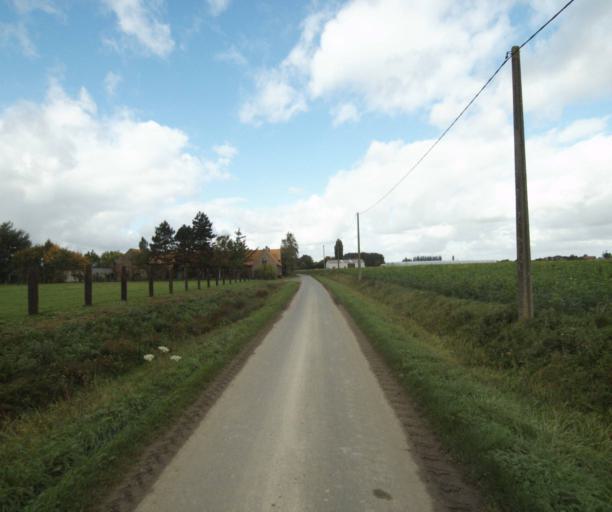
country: FR
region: Nord-Pas-de-Calais
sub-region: Departement du Nord
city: Perenchies
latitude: 50.6958
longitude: 2.9600
